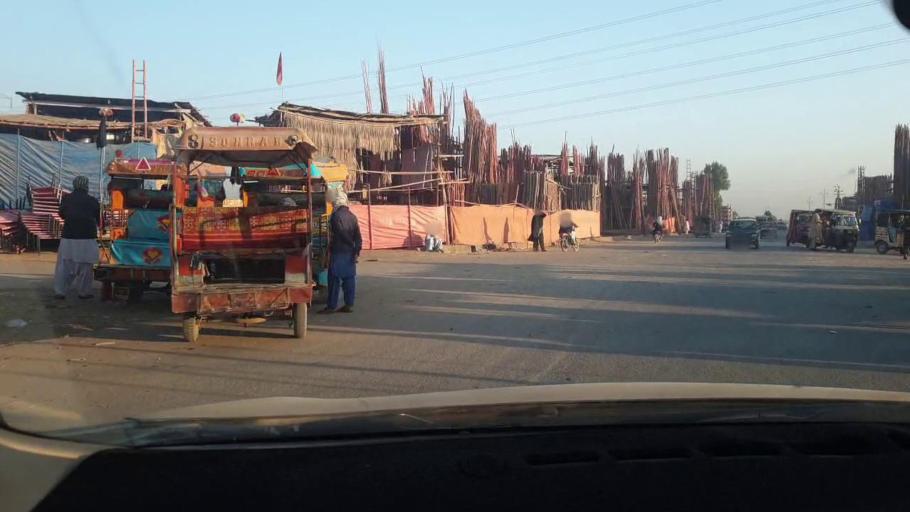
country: PK
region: Sindh
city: Malir Cantonment
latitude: 24.9955
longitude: 67.1422
